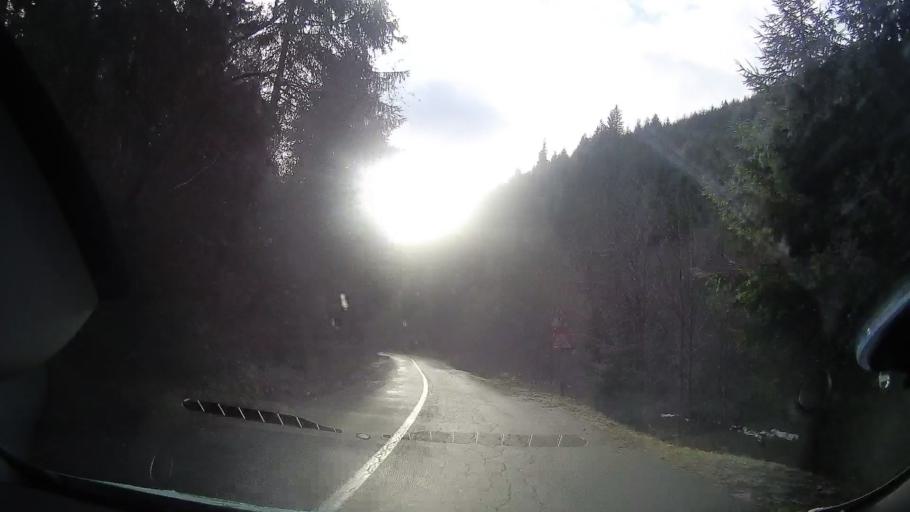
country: RO
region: Alba
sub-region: Comuna Albac
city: Albac
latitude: 46.4741
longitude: 22.9632
